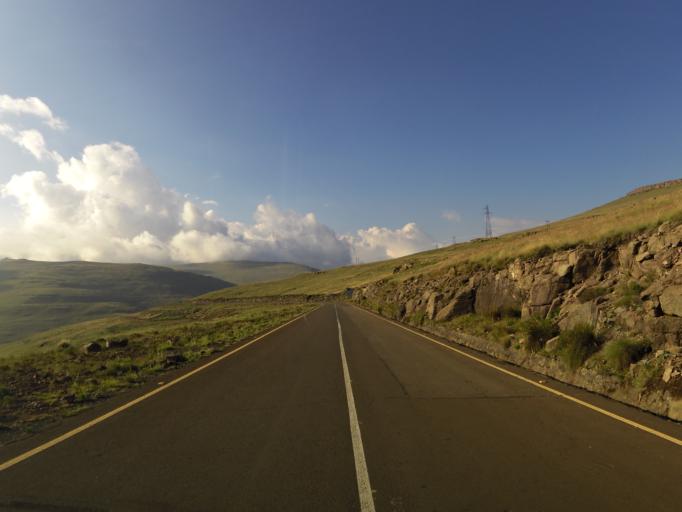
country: LS
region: Butha-Buthe
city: Butha-Buthe
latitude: -29.1014
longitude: 28.4249
